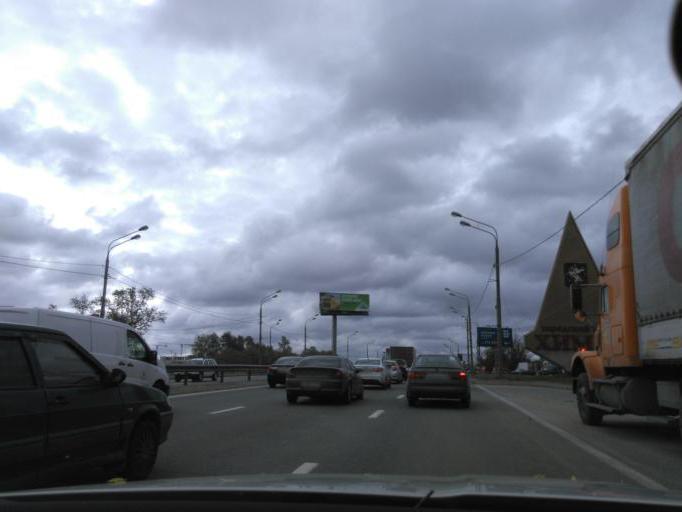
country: RU
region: Moskovskaya
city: Novopodrezkovo
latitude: 55.9364
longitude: 37.3704
